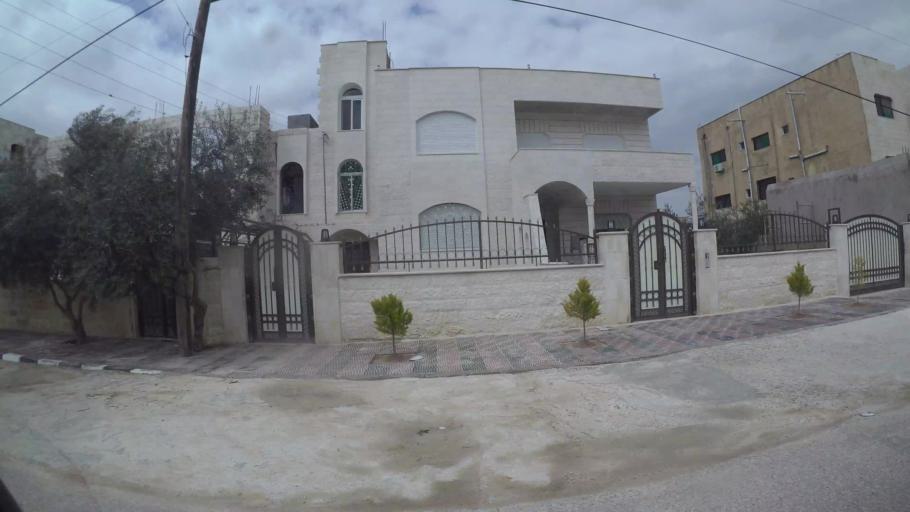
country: JO
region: Amman
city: Al Jubayhah
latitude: 32.0495
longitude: 35.8259
